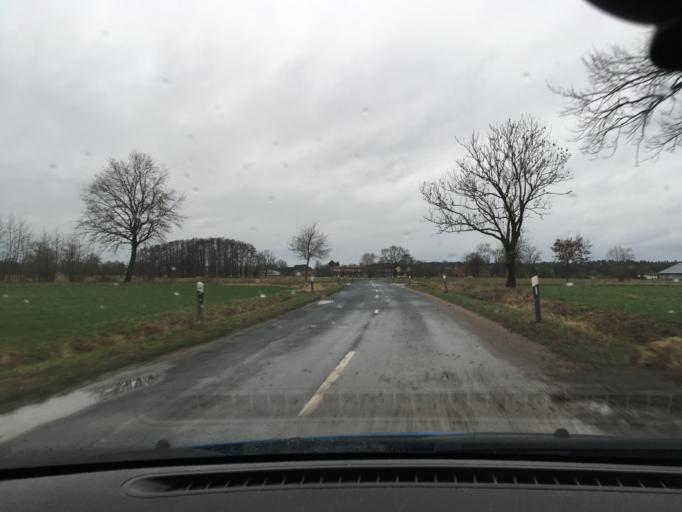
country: DE
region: Schleswig-Holstein
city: Lanze
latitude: 53.3633
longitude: 10.6378
